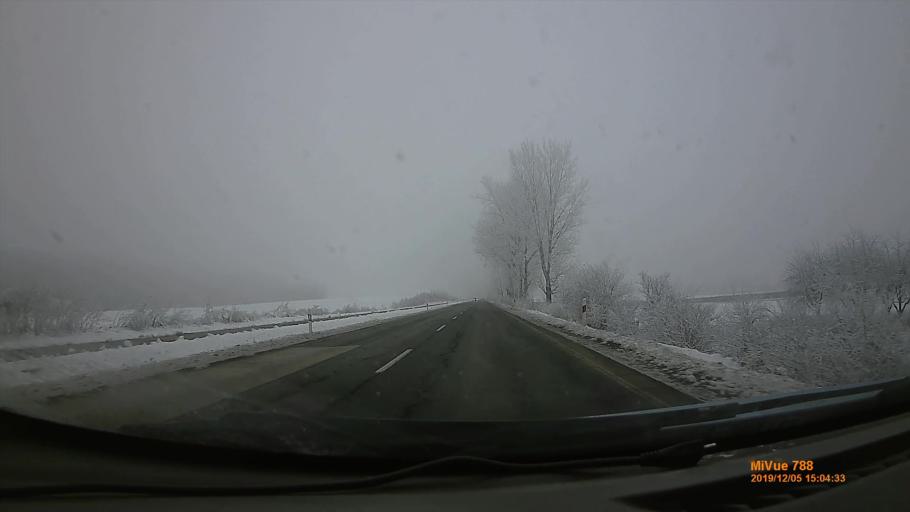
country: HU
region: Szabolcs-Szatmar-Bereg
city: Tiszanagyfalu
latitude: 48.0983
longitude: 21.4923
